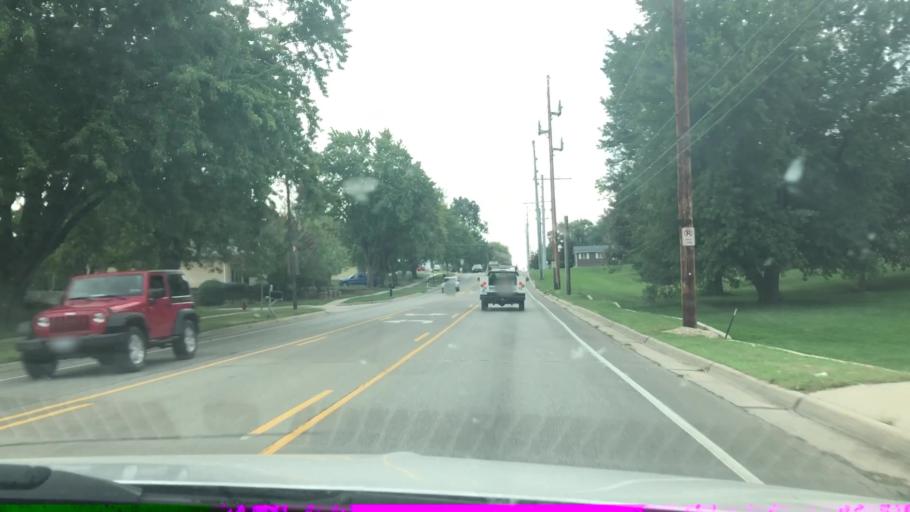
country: US
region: Iowa
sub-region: Marshall County
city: Marshalltown
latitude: 42.0227
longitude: -92.9221
